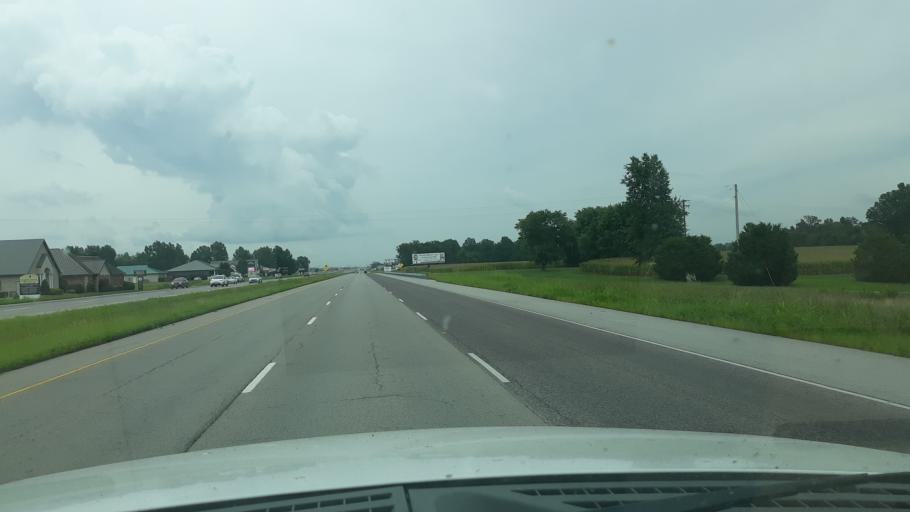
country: US
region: Illinois
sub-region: Williamson County
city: Energy
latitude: 37.7450
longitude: -89.0321
